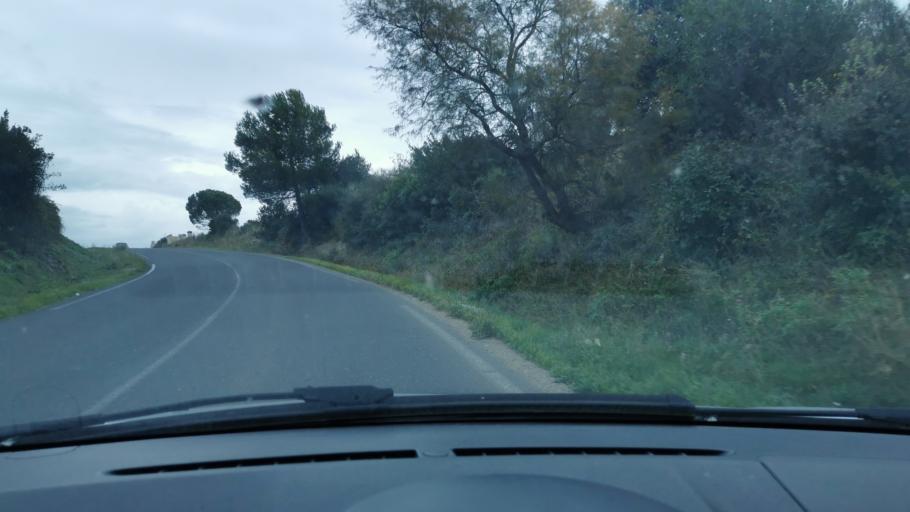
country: FR
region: Languedoc-Roussillon
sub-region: Departement de l'Herault
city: Balaruc-les-Bains
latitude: 43.4366
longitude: 3.7083
